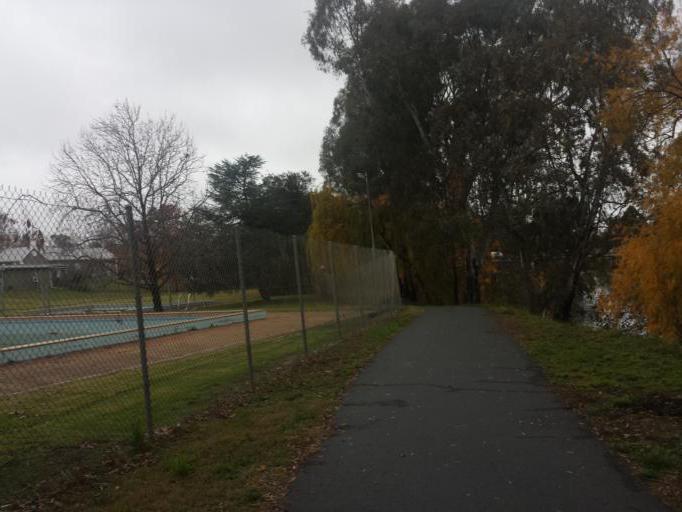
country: AU
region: Victoria
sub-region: Benalla
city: Benalla
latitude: -36.5510
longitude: 145.9801
